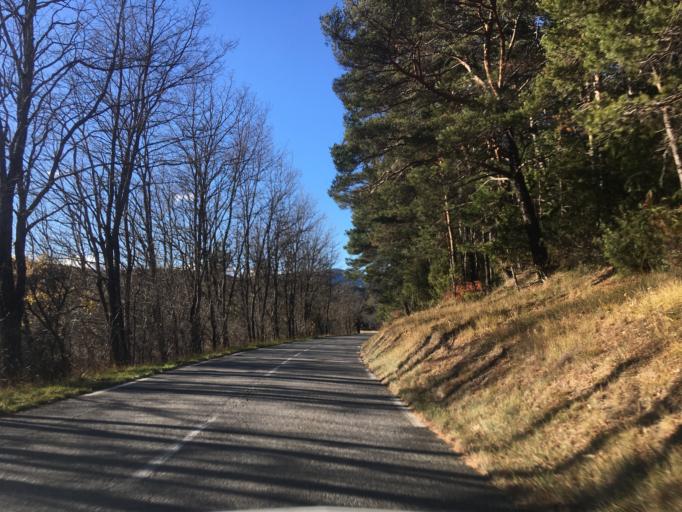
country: FR
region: Provence-Alpes-Cote d'Azur
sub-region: Departement des Alpes-de-Haute-Provence
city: Castellane
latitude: 43.7409
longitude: 6.4851
